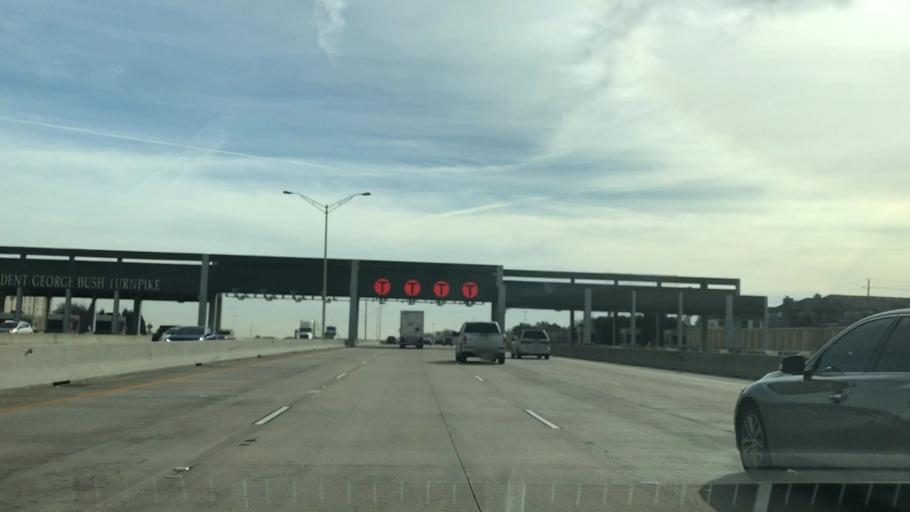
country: US
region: Texas
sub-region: Dallas County
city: Addison
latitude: 33.0030
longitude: -96.7773
